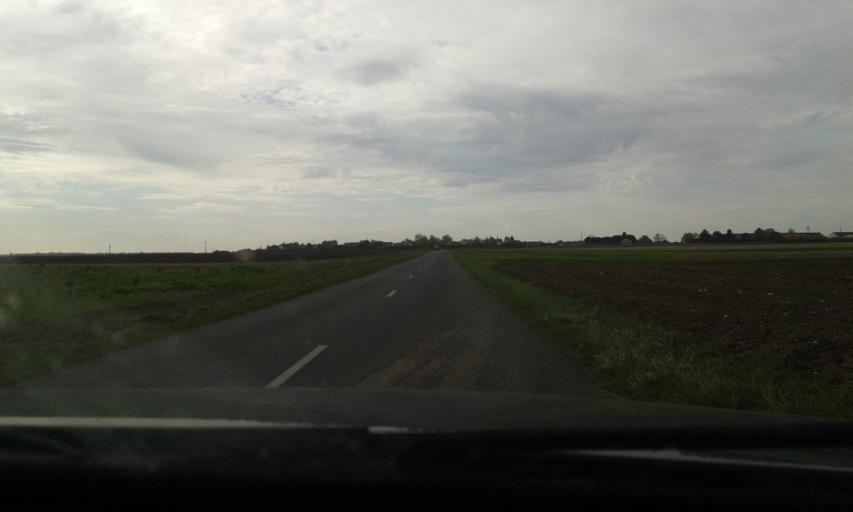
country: FR
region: Centre
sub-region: Departement du Loiret
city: Bricy
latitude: 47.9869
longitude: 1.7949
